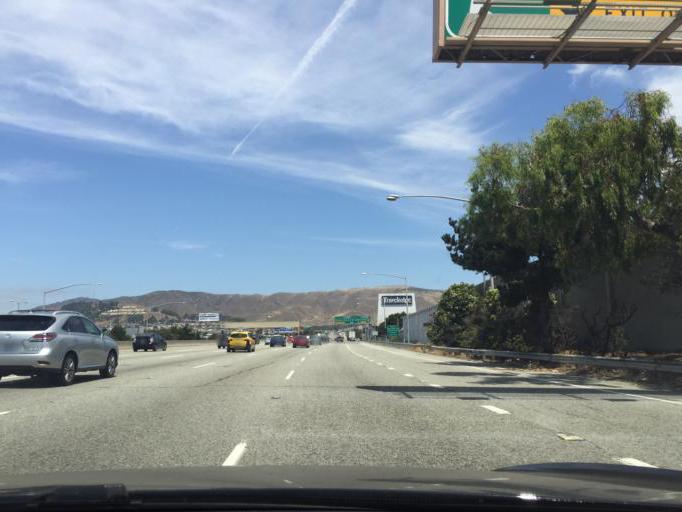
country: US
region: California
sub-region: San Mateo County
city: San Bruno
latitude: 37.6417
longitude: -122.4058
